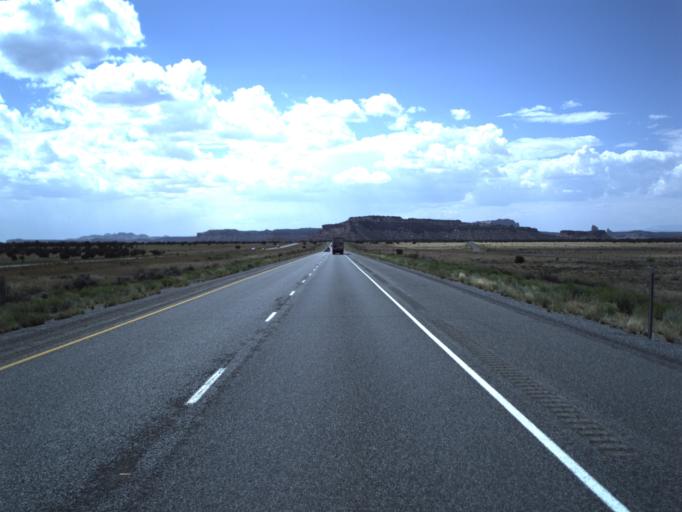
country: US
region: Utah
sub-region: Emery County
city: Castle Dale
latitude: 38.8939
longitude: -110.6225
